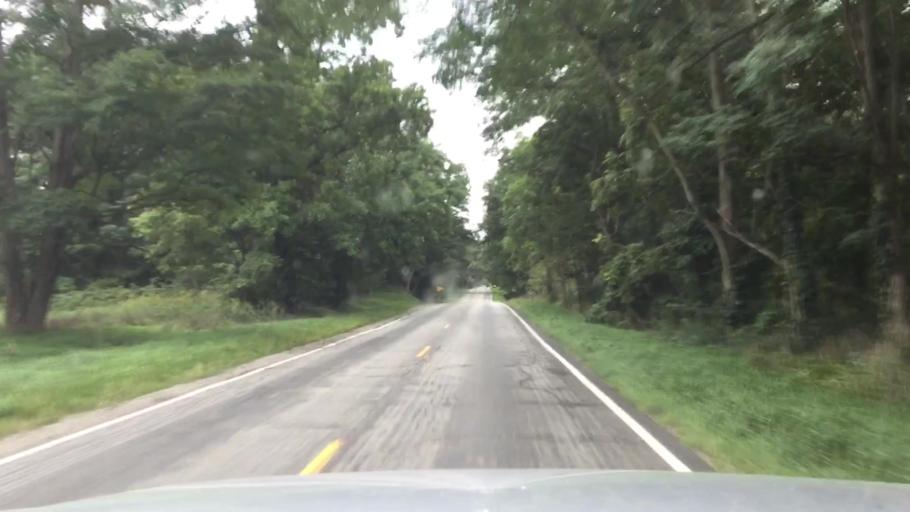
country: US
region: Michigan
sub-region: Genesee County
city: Argentine
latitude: 42.8137
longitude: -83.9059
